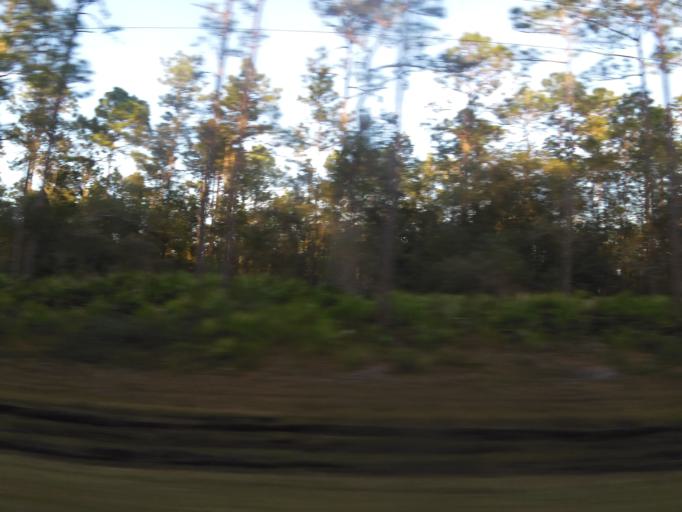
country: US
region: Florida
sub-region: Clay County
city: Green Cove Springs
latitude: 29.8741
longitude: -81.5500
